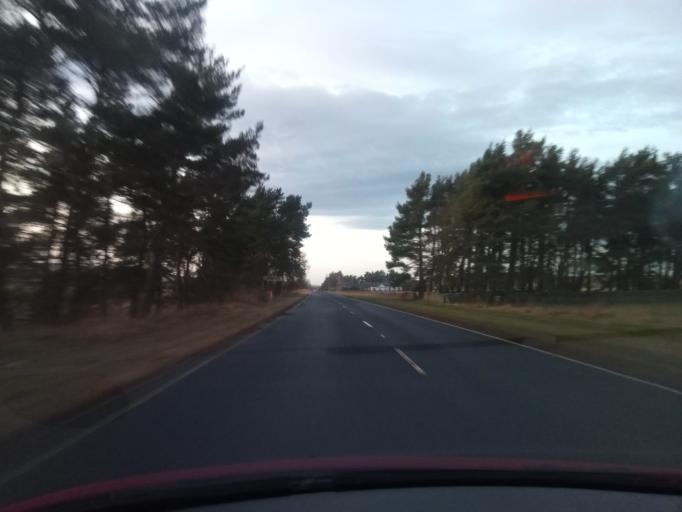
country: GB
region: England
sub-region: Northumberland
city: Otterburn
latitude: 55.2358
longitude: -2.1947
